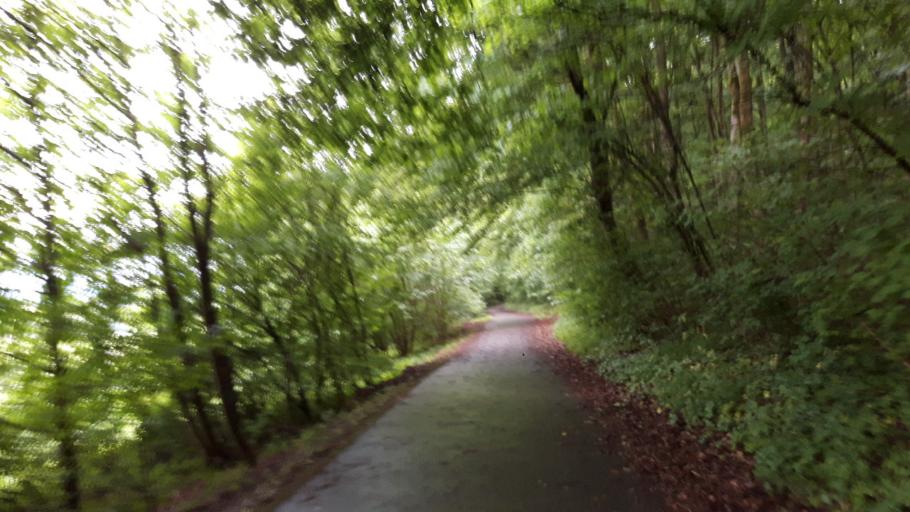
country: DE
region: Thuringia
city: Hildburghausen
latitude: 50.4133
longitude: 10.7609
